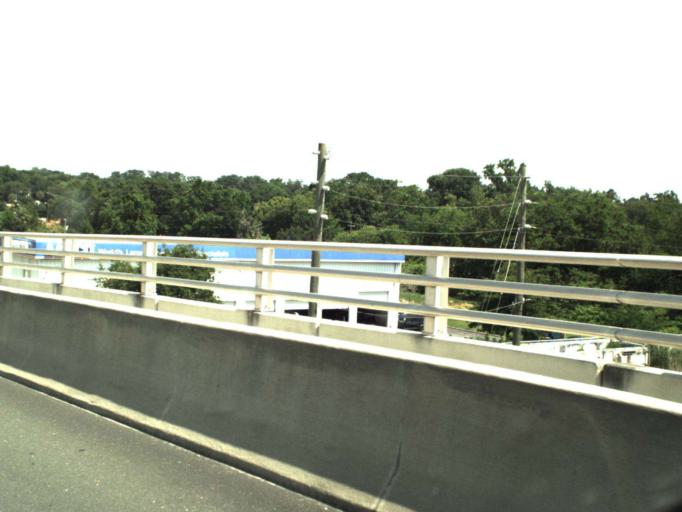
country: US
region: Florida
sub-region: Marion County
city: Ocala
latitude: 29.1716
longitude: -82.1437
